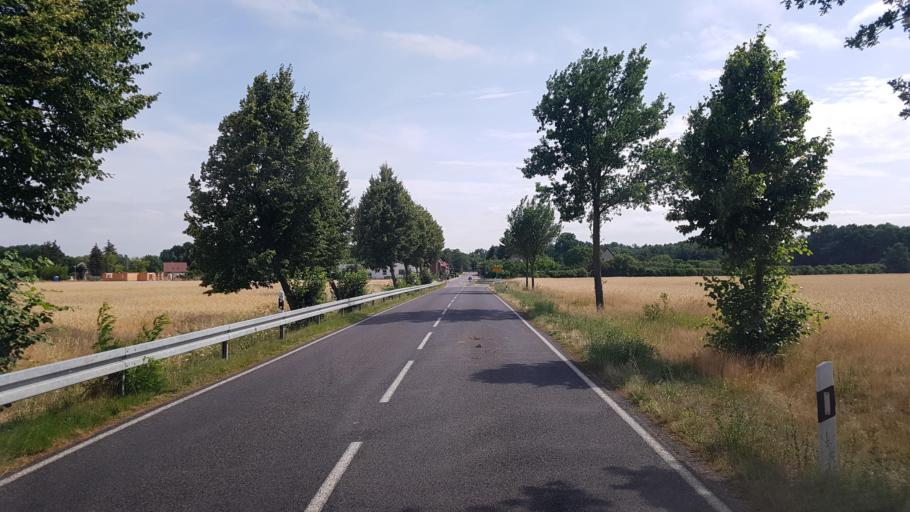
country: DE
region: Saxony-Anhalt
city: Muhlanger
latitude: 51.8598
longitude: 12.7489
